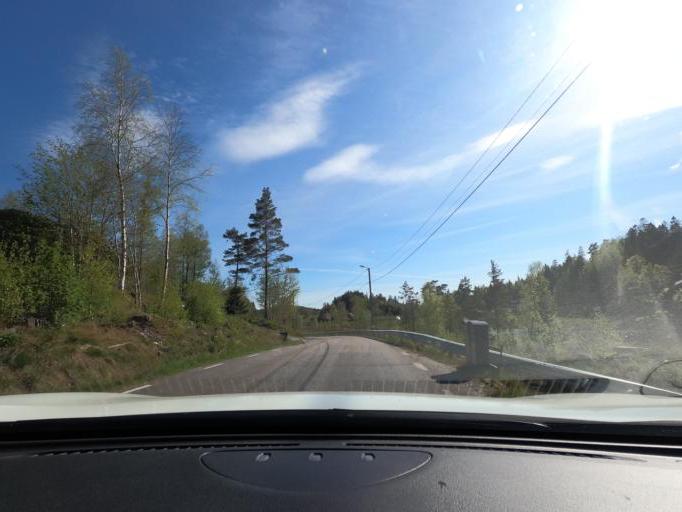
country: SE
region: Vaestra Goetaland
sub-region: Harryda Kommun
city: Hindas
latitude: 57.6435
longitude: 12.3520
